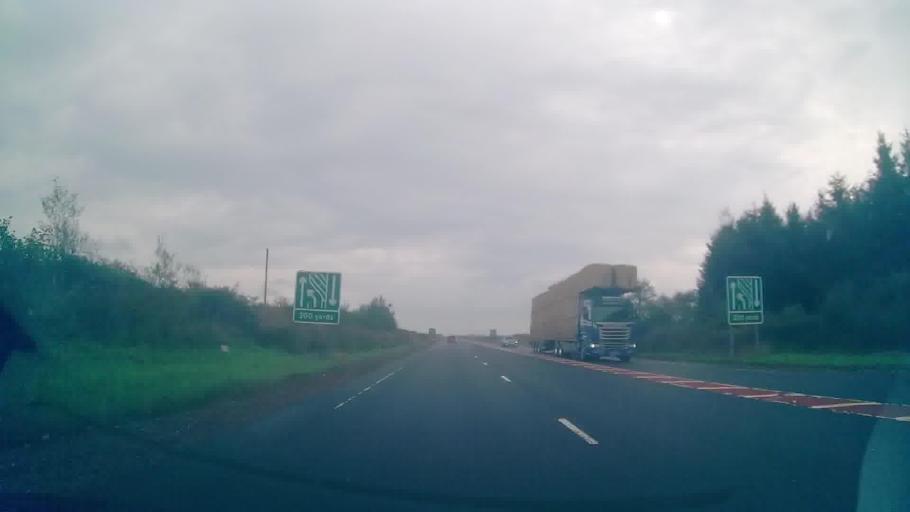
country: GB
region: Scotland
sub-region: Dumfries and Galloway
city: Lockerbie
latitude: 55.0226
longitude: -3.3742
